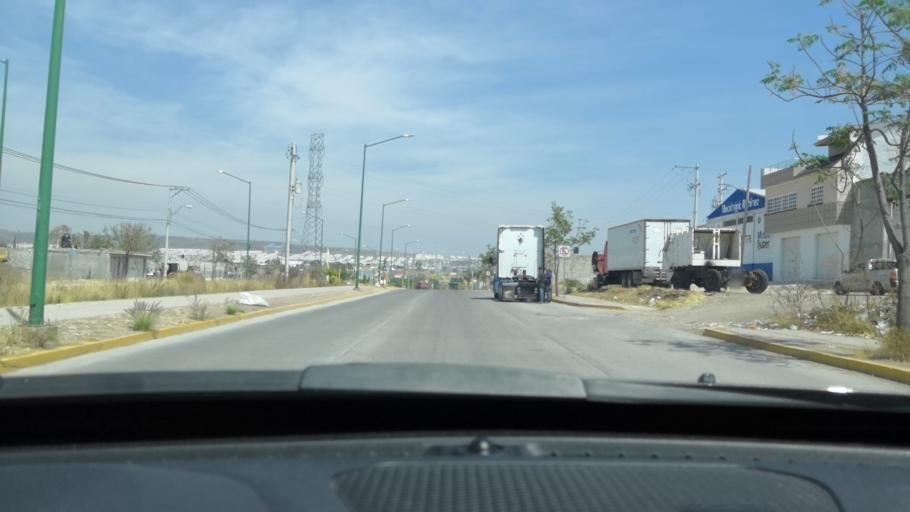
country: MX
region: Guanajuato
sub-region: Leon
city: Ejido la Joya
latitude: 21.1359
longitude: -101.7350
